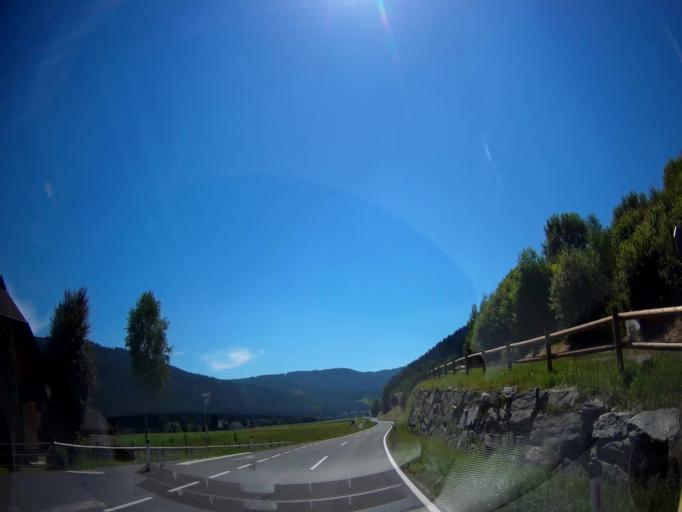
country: AT
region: Carinthia
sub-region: Politischer Bezirk Sankt Veit an der Glan
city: Gurk
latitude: 46.8586
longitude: 14.2204
